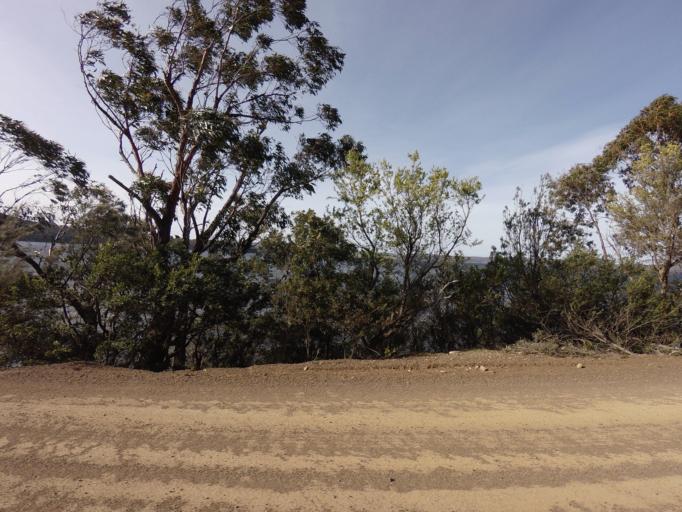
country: AU
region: Tasmania
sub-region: Kingborough
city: Kettering
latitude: -43.1152
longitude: 147.2714
